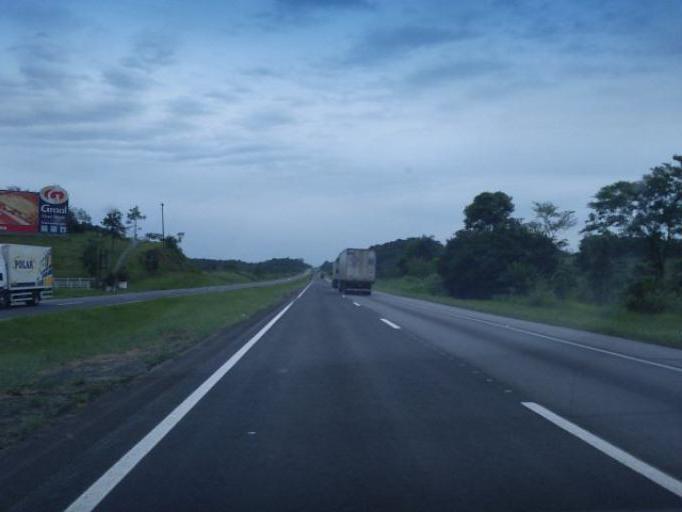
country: BR
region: Sao Paulo
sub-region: Registro
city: Registro
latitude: -24.4288
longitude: -47.7848
